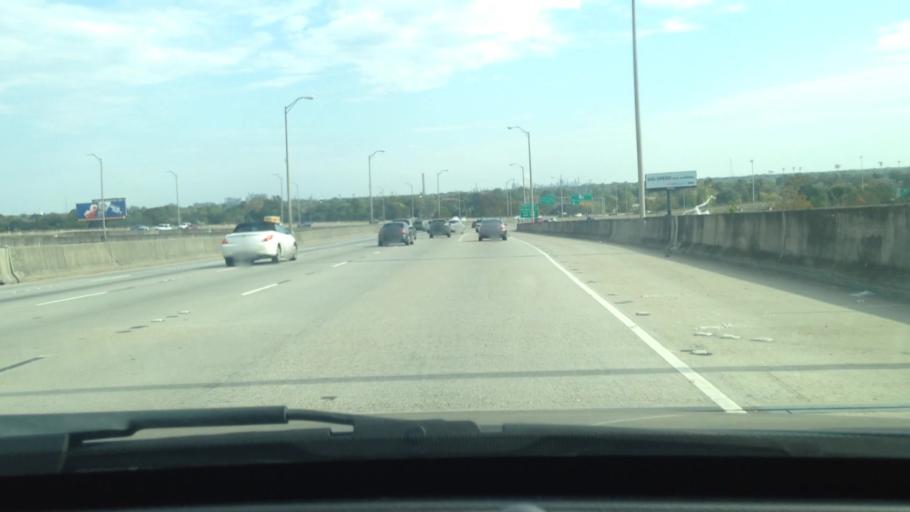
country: US
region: Louisiana
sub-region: Jefferson Parish
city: Gretna
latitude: 29.9378
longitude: -90.0441
